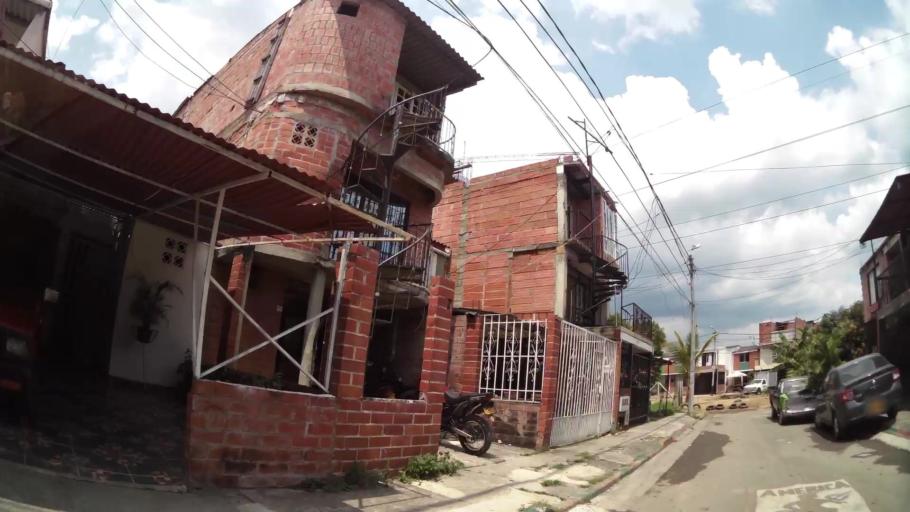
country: CO
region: Valle del Cauca
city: Cali
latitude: 3.4580
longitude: -76.4684
